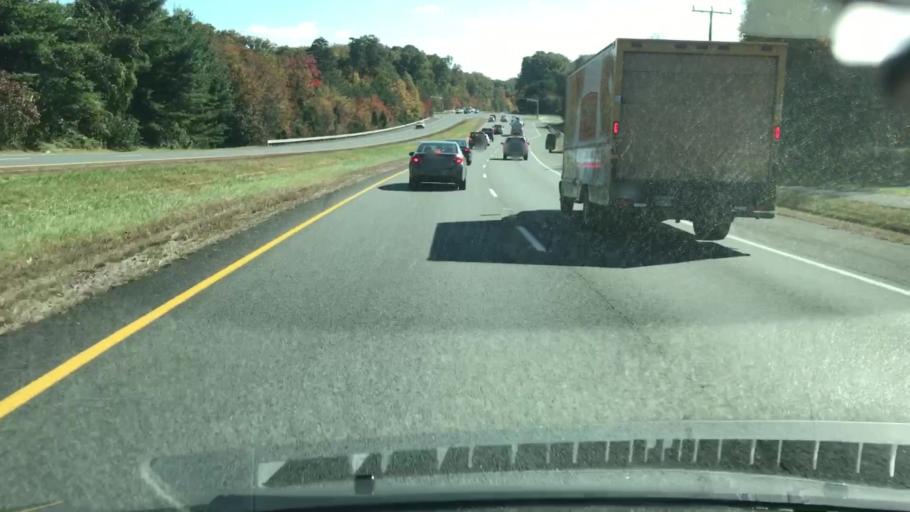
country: US
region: Virginia
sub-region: Fairfax County
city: Burke
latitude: 38.7783
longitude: -77.3001
